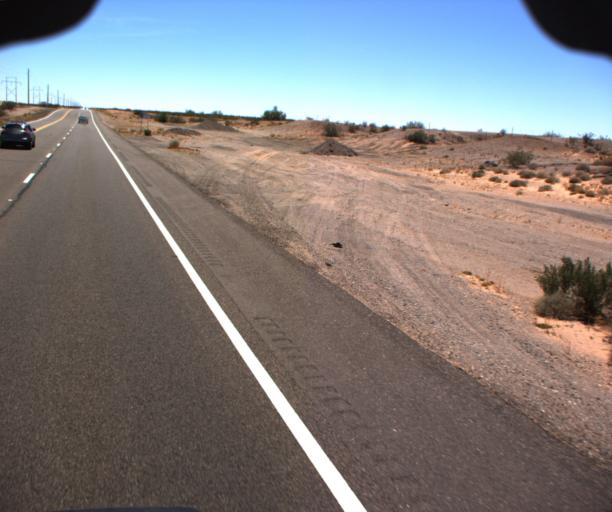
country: US
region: Arizona
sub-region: La Paz County
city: Parker
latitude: 33.9849
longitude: -114.2169
